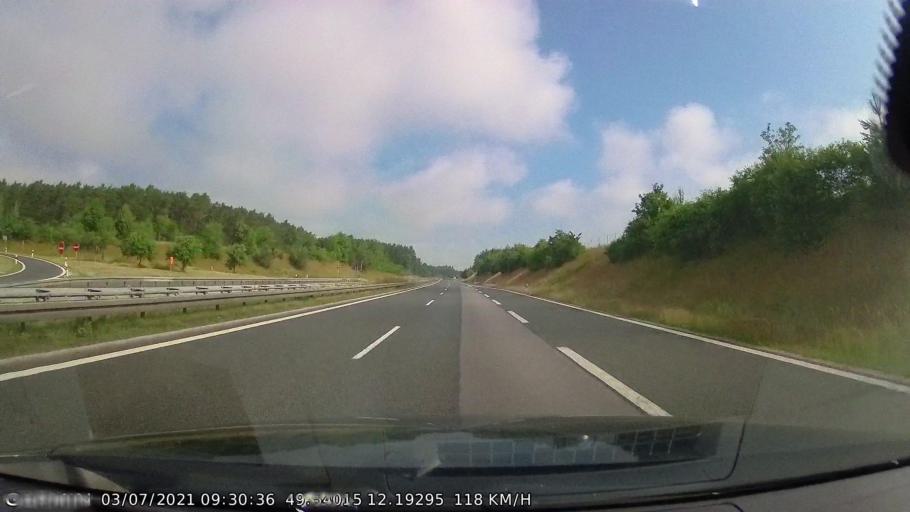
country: DE
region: Bavaria
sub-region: Upper Palatinate
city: Wernberg-Koblitz
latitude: 49.5400
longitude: 12.1929
